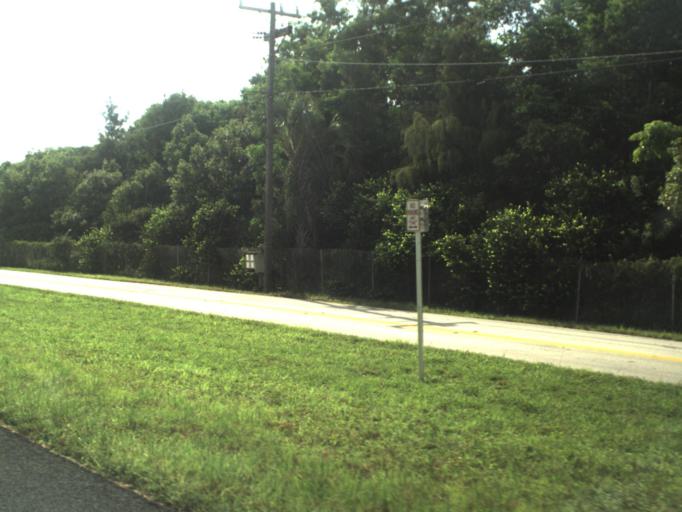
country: US
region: Florida
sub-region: Broward County
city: Broadview Park
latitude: 26.0847
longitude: -80.1880
